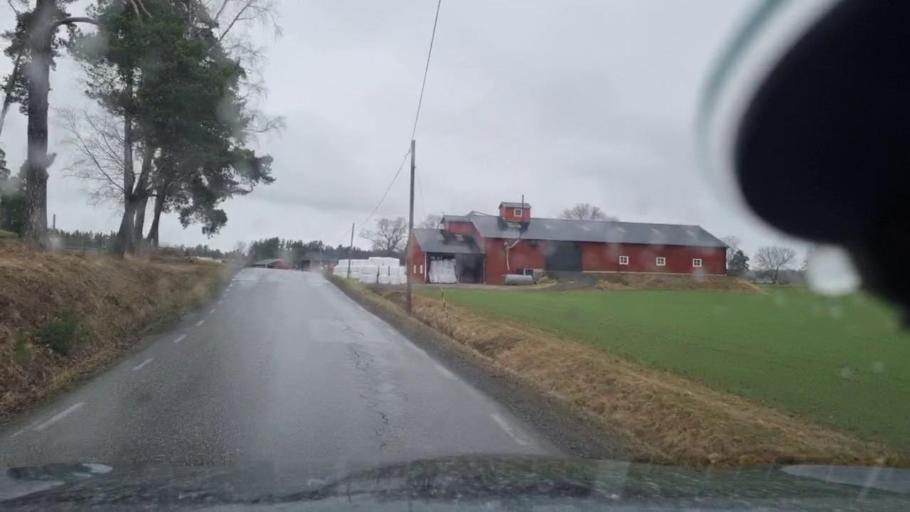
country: SE
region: Stockholm
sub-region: Vallentuna Kommun
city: Vallentuna
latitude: 59.5301
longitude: 18.0411
